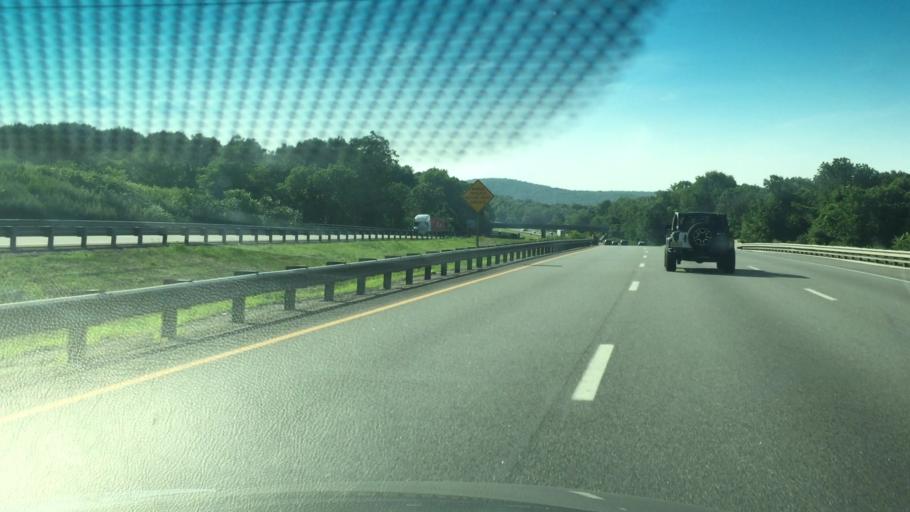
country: US
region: New Jersey
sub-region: Sussex County
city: Stanhope
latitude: 40.9050
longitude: -74.7236
